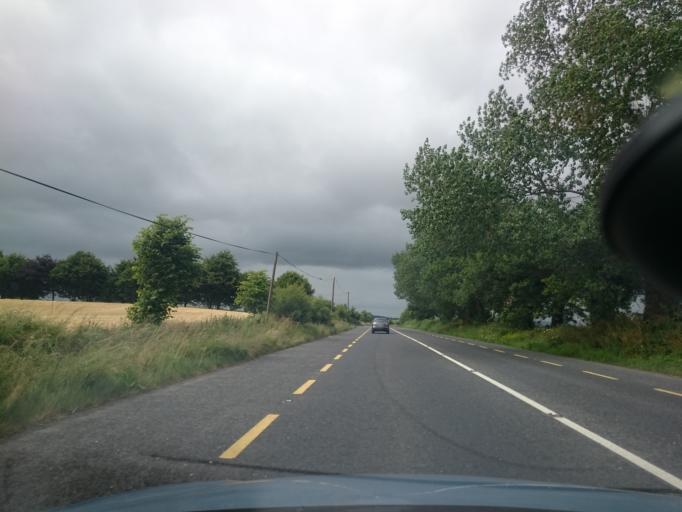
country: IE
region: Leinster
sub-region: Kildare
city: Castledermot
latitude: 52.8658
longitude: -6.8746
